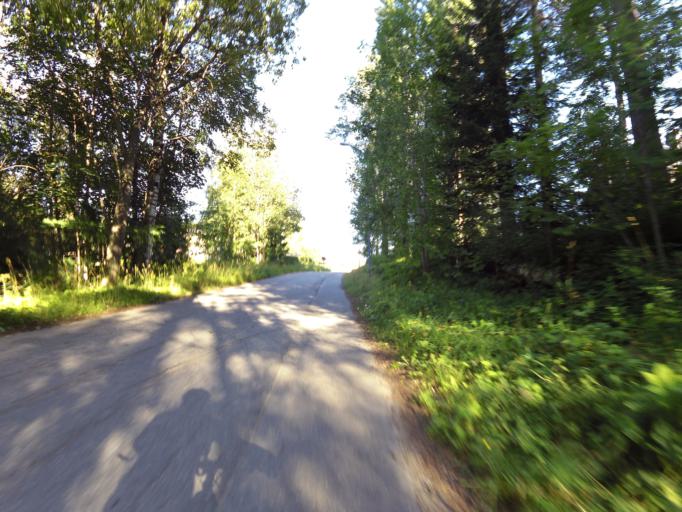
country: SE
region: Gaevleborg
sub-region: Hofors Kommun
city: Hofors
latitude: 60.5710
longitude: 16.2653
